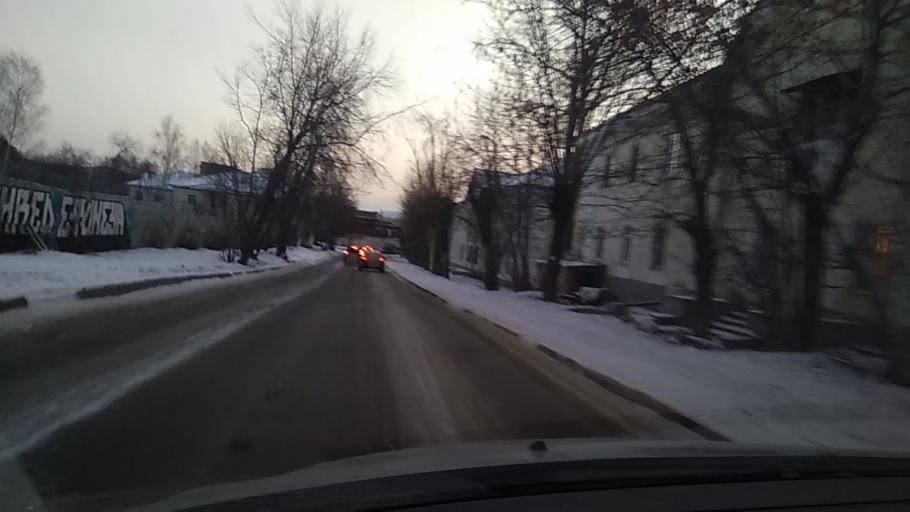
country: RU
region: Sverdlovsk
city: Istok
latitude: 56.7601
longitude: 60.7118
